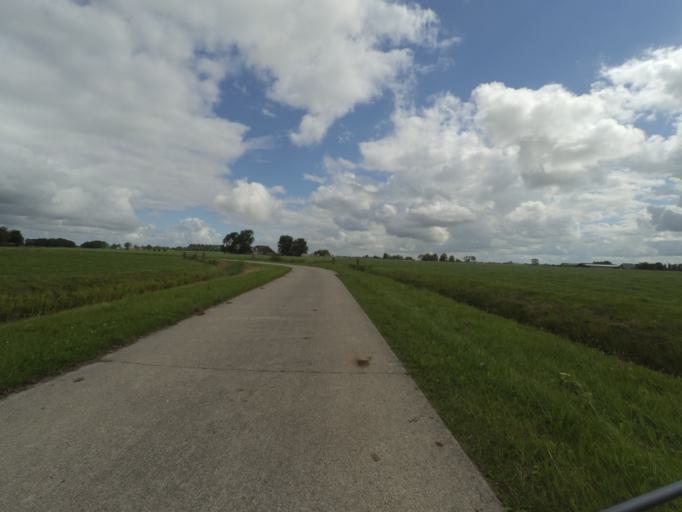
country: NL
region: Friesland
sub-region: Gemeente Kollumerland en Nieuwkruisland
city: Kollum
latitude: 53.2867
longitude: 6.2269
